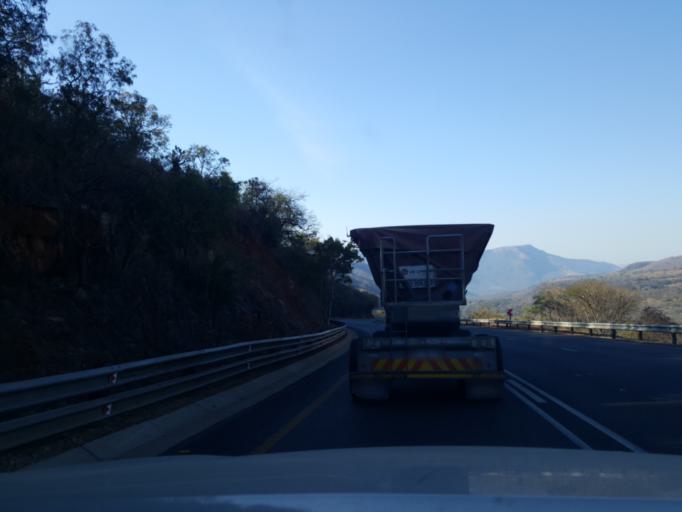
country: ZA
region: Mpumalanga
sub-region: Ehlanzeni District
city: Lydenburg
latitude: -25.4308
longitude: 30.4797
